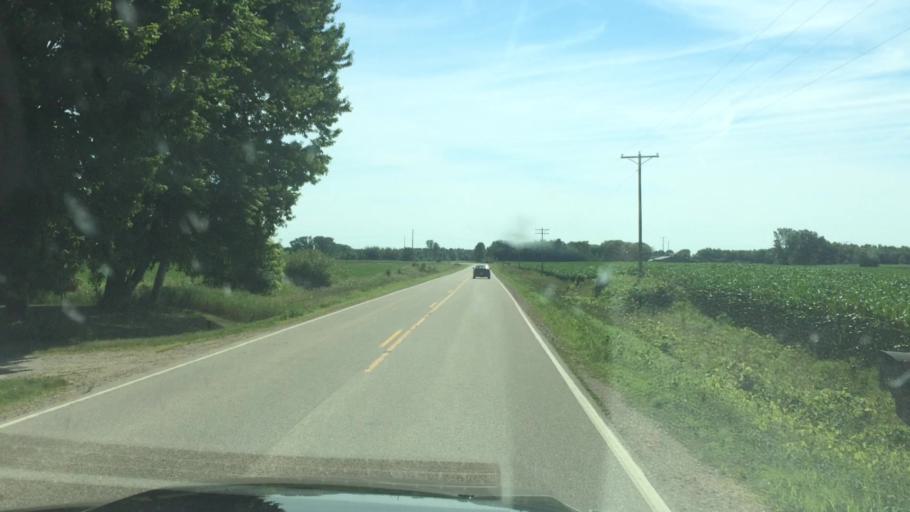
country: US
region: Wisconsin
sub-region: Oconto County
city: Gillett
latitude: 44.7876
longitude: -88.3203
